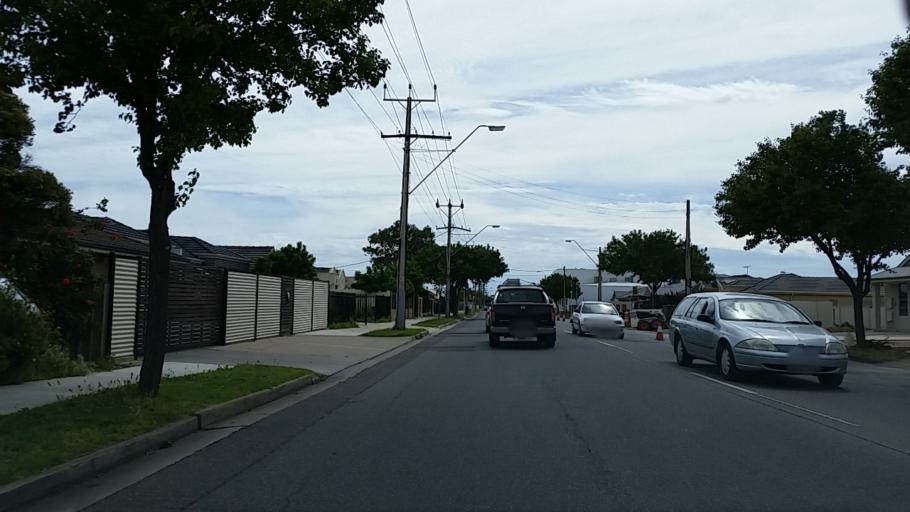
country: AU
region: South Australia
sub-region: Charles Sturt
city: Seaton
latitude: -34.8915
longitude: 138.5218
